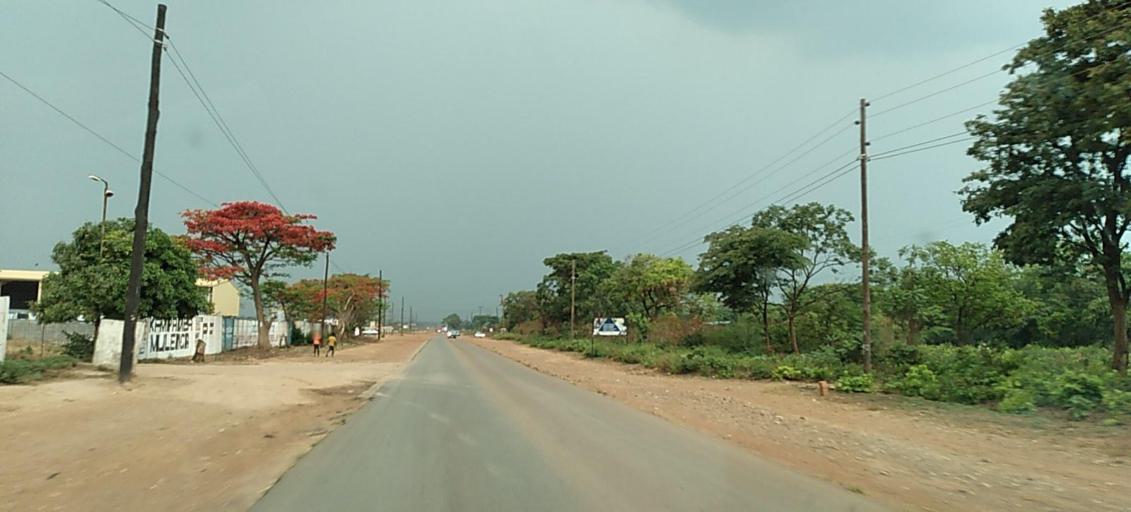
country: ZM
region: Copperbelt
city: Kalulushi
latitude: -12.8334
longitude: 28.1081
